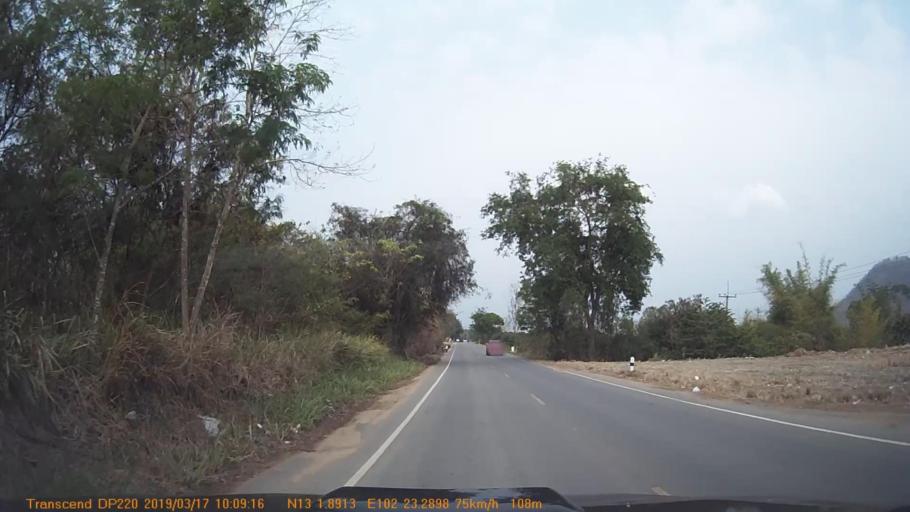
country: TH
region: Chanthaburi
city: Pong Nam Ron
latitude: 13.0320
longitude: 102.3860
